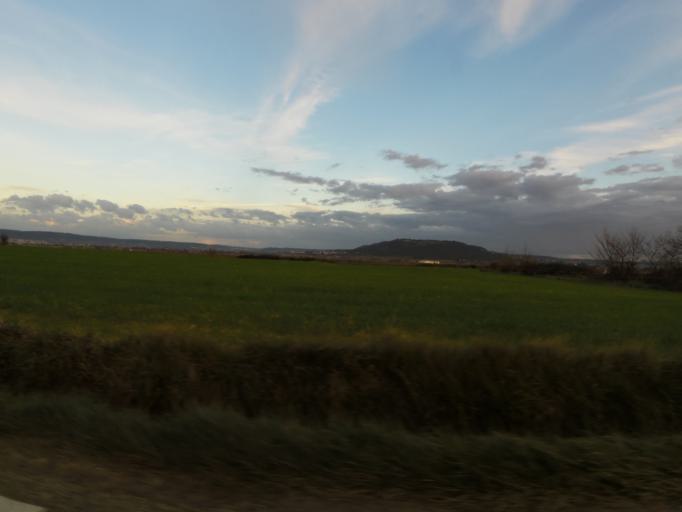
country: FR
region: Languedoc-Roussillon
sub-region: Departement du Gard
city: Calvisson
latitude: 43.7982
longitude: 4.1932
